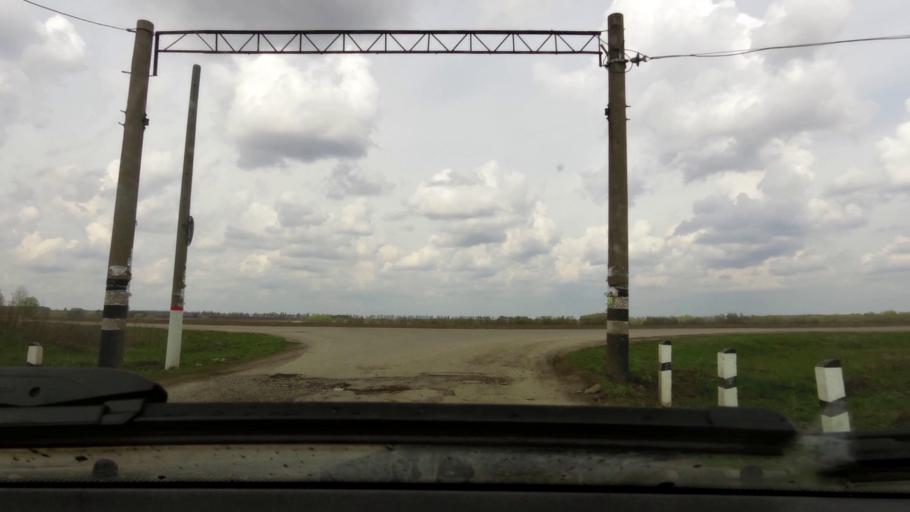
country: RU
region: Rjazan
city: Bagramovo
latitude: 54.7073
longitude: 39.3145
